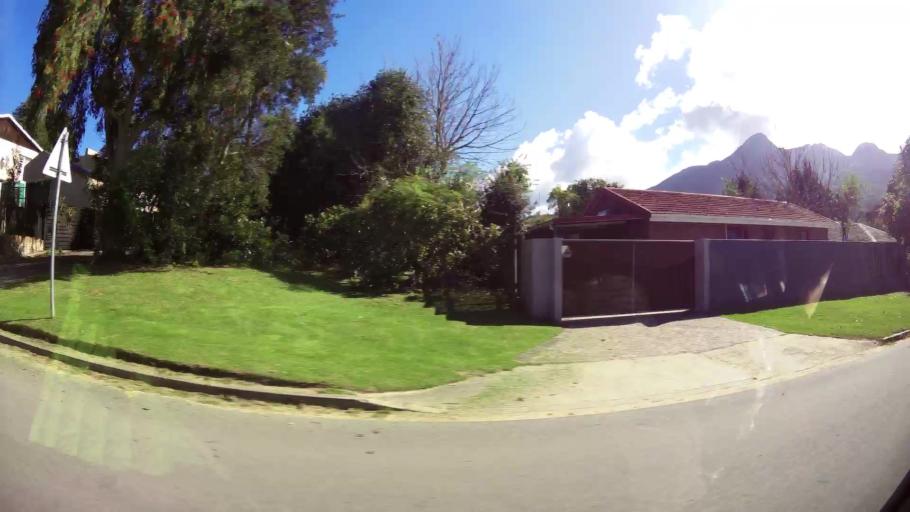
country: ZA
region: Western Cape
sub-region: Eden District Municipality
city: George
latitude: -33.9466
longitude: 22.4688
